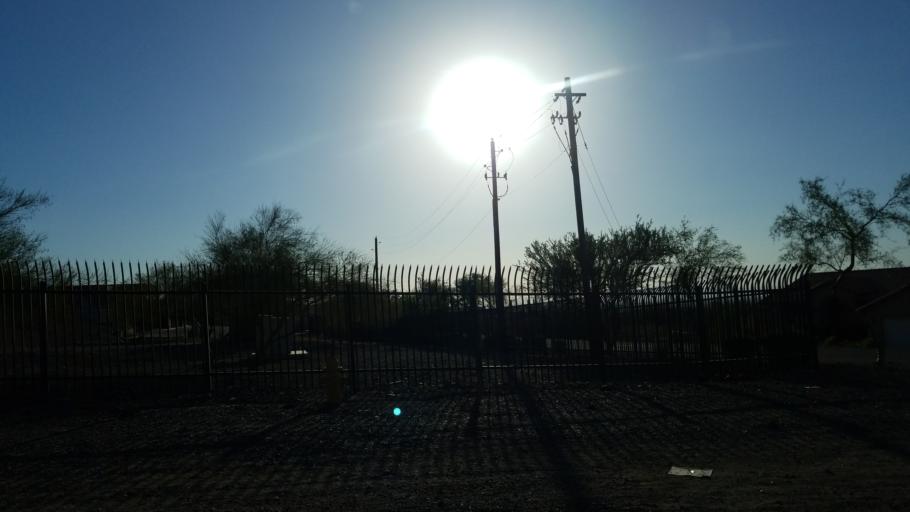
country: US
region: Arizona
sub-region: Maricopa County
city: Laveen
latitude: 33.3486
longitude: -112.1178
